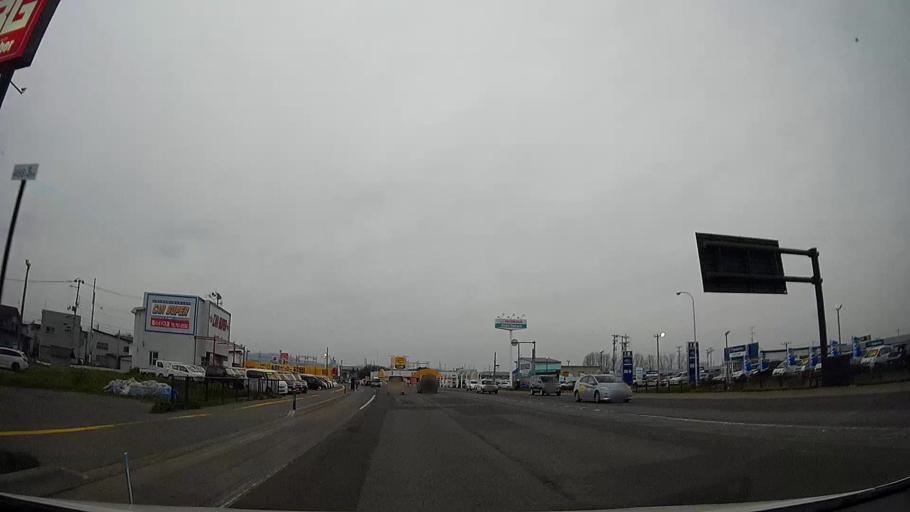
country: JP
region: Aomori
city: Aomori Shi
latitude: 40.8327
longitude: 140.7001
